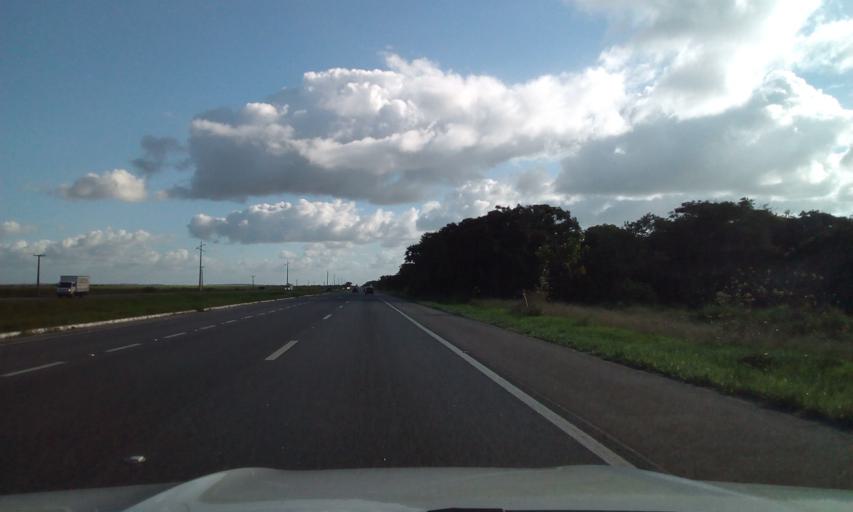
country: BR
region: Paraiba
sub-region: Cruz Do Espirito Santo
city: Cruz do Espirito Santo
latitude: -7.1631
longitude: -35.0244
